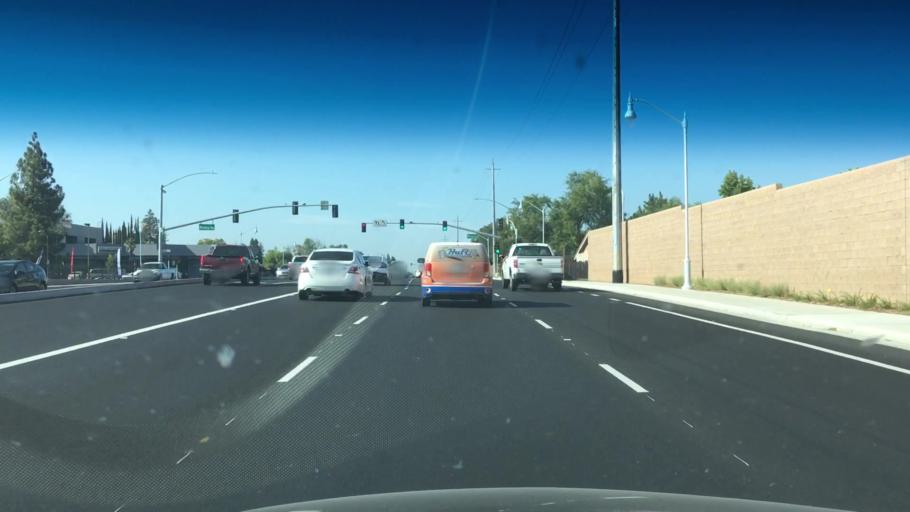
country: US
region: California
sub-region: Sacramento County
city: Gold River
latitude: 38.6452
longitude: -121.2254
